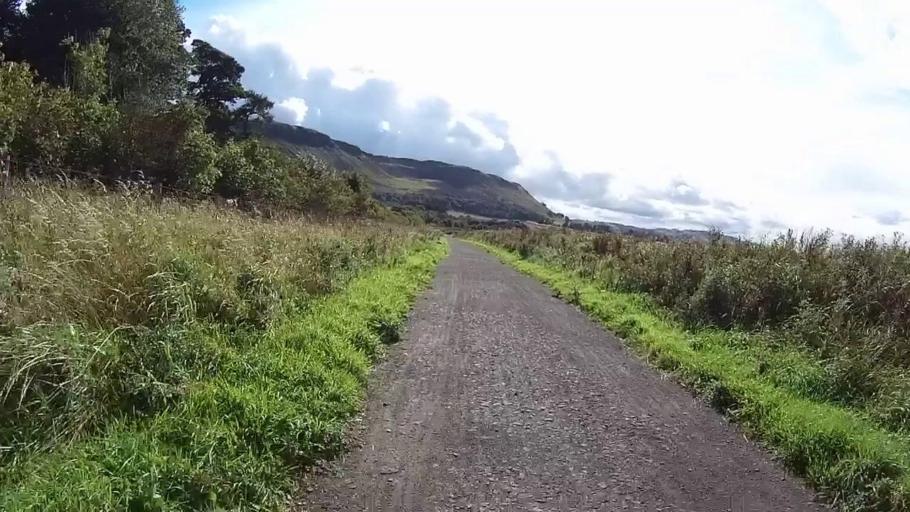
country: GB
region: Scotland
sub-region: Fife
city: Ballingry
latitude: 56.1769
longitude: -3.3555
